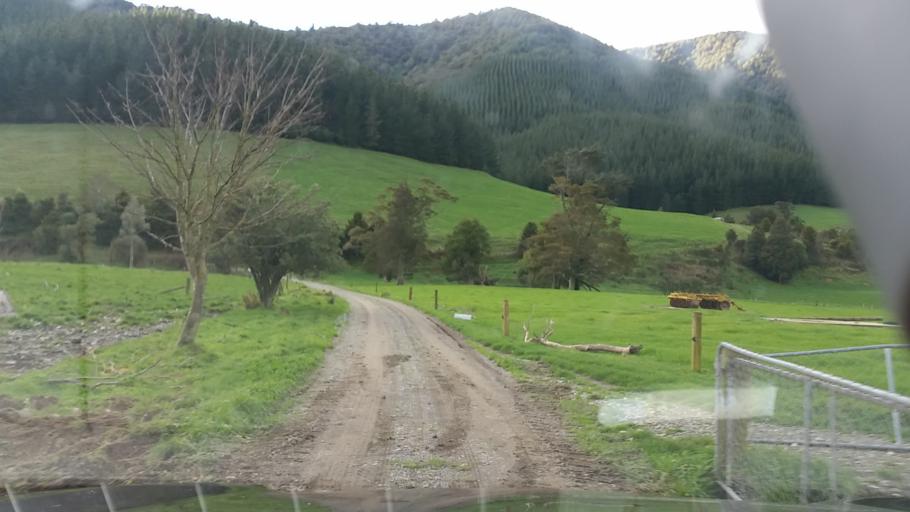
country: NZ
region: Nelson
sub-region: Nelson City
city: Nelson
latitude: -41.2103
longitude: 173.6425
